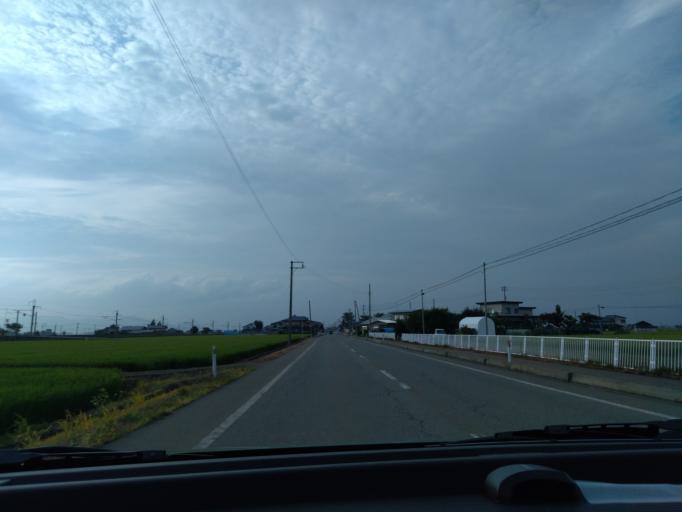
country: JP
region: Akita
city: Omagari
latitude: 39.3962
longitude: 140.5220
